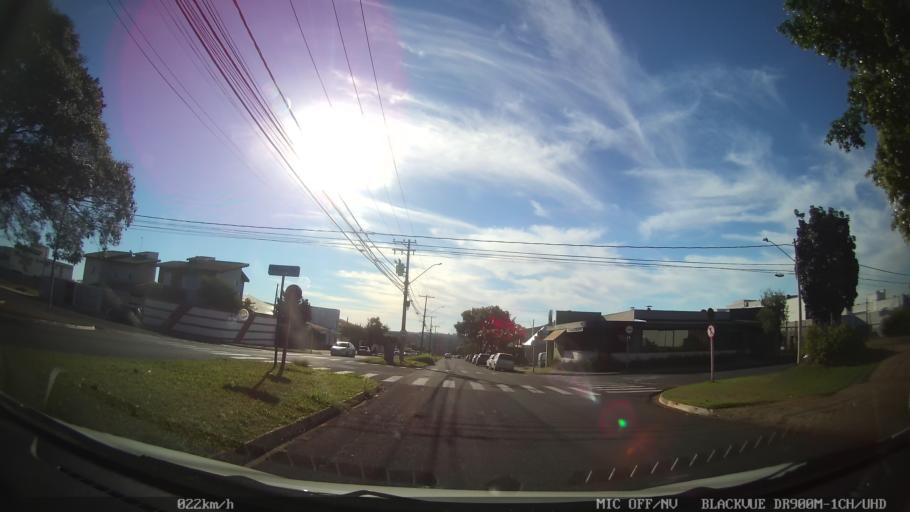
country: BR
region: Sao Paulo
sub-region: Araraquara
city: Araraquara
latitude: -21.7659
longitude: -48.1731
